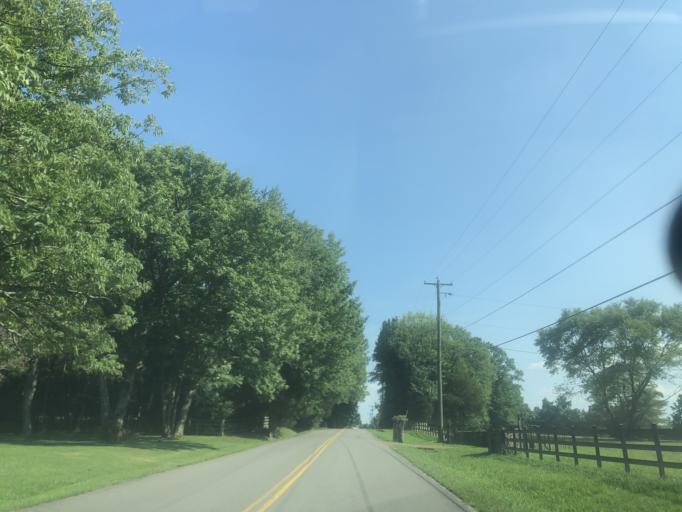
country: US
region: Tennessee
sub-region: Wilson County
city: Green Hill
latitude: 36.1447
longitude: -86.5954
